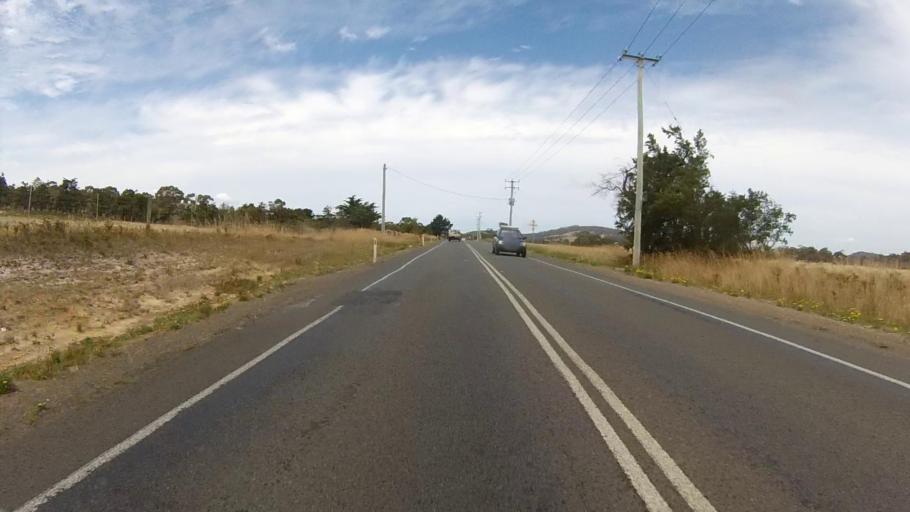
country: AU
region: Tasmania
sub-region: Clarence
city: Sandford
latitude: -42.9309
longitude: 147.4910
